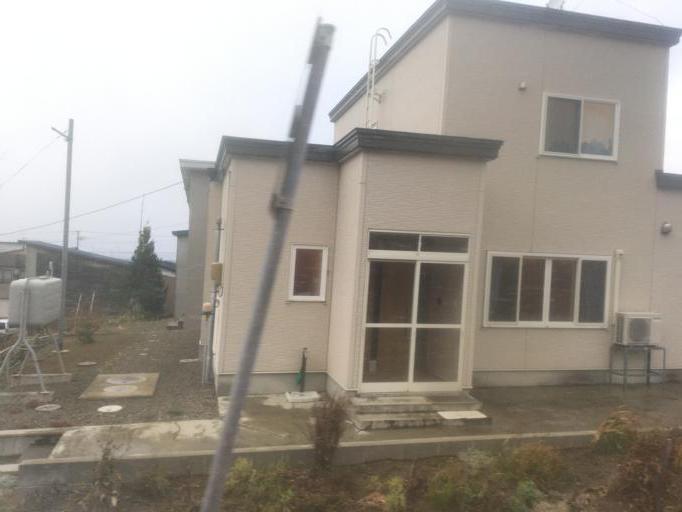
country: JP
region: Aomori
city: Goshogawara
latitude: 41.1815
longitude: 140.4816
